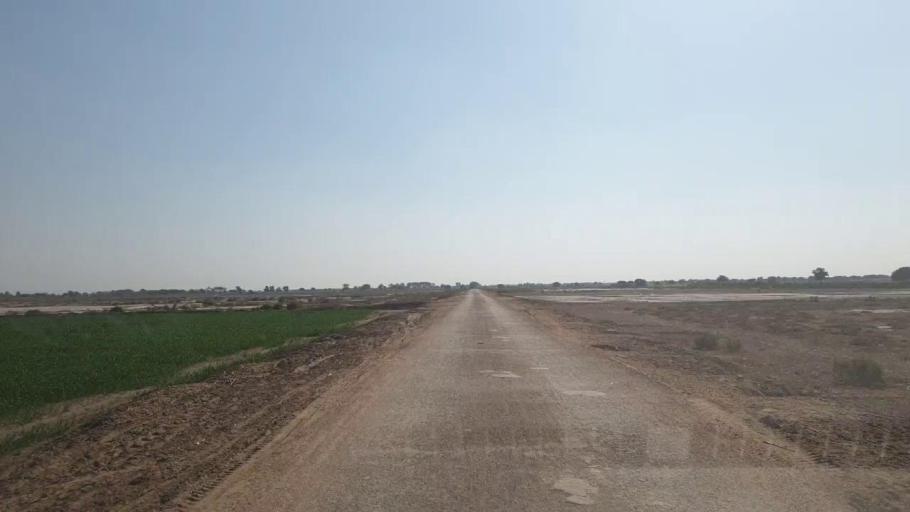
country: PK
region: Sindh
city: Chambar
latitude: 25.3009
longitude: 68.7418
